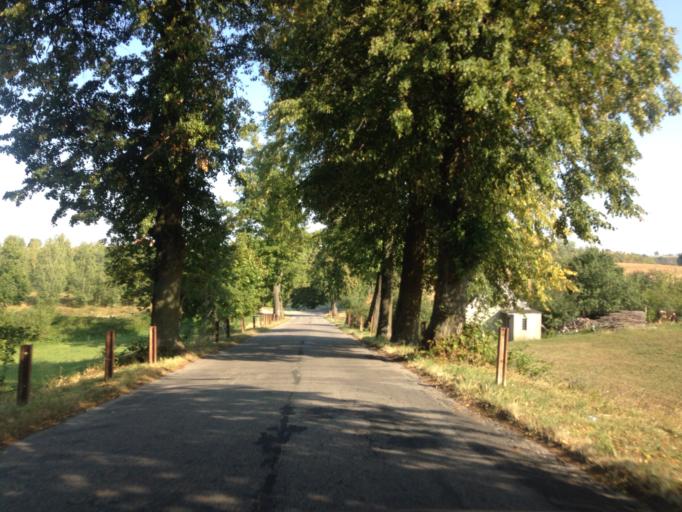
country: PL
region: Kujawsko-Pomorskie
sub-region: Powiat brodnicki
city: Brzozie
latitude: 53.3020
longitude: 19.6148
